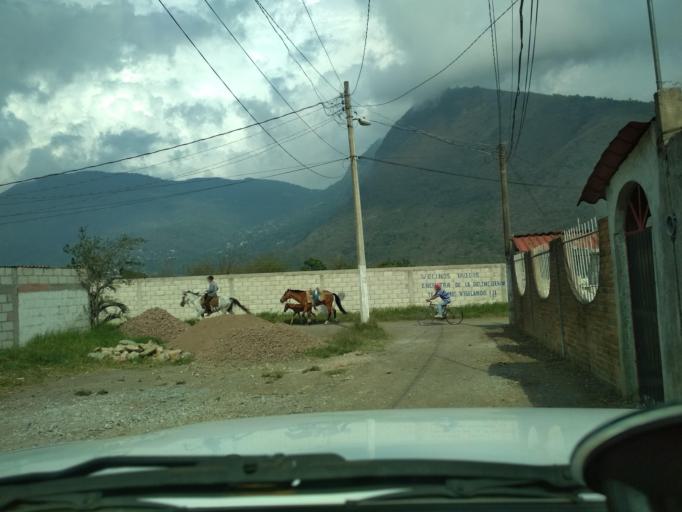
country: MX
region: Veracruz
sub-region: Nogales
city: Taza de Agua Ojo Zarco
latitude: 18.7964
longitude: -97.1959
